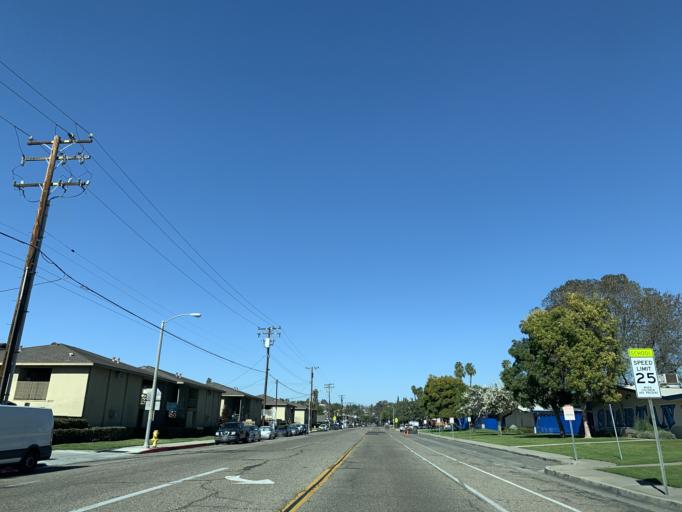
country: US
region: California
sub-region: Orange County
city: Fullerton
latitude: 33.8708
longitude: -117.8983
